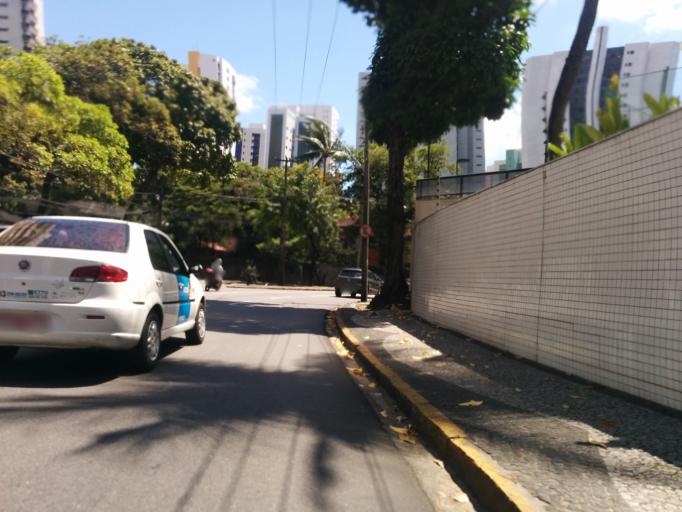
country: BR
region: Pernambuco
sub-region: Recife
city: Recife
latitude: -8.0340
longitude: -34.9071
